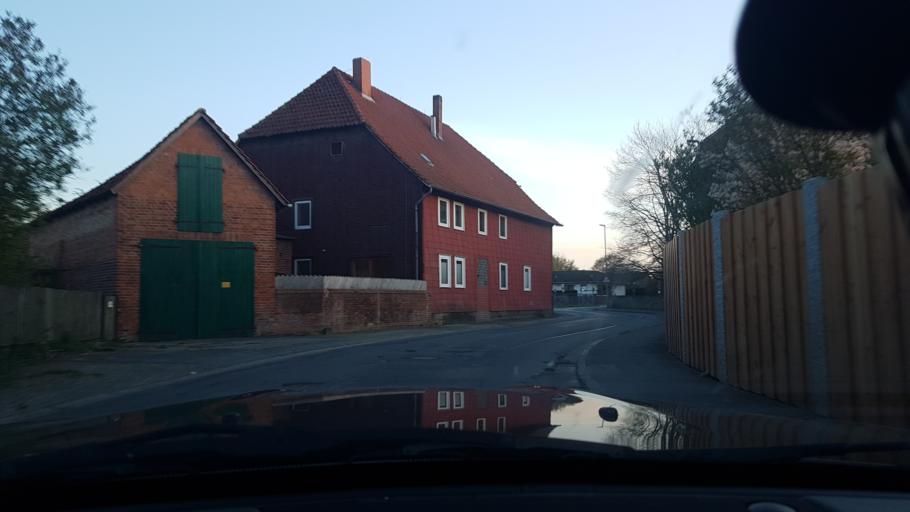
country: DE
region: Lower Saxony
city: Hemmingen
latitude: 52.2820
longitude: 9.7124
